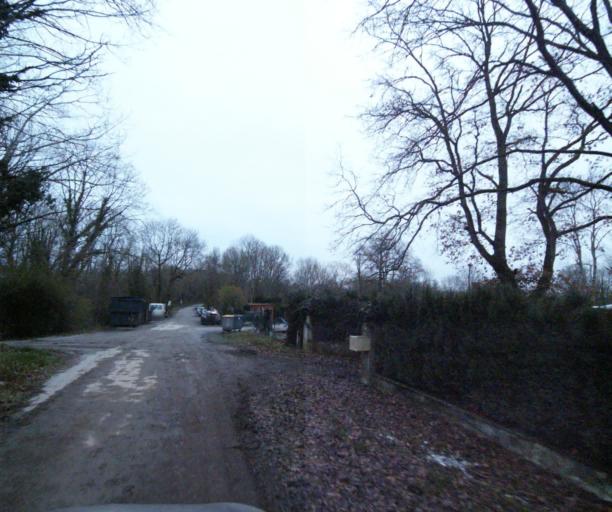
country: FR
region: Ile-de-France
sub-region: Departement de Seine-et-Marne
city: Longperrier
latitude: 49.0642
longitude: 2.6543
